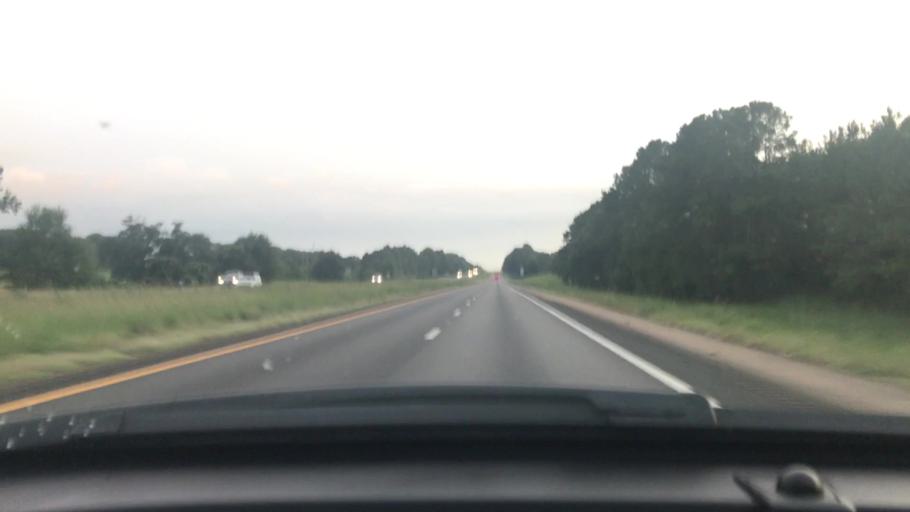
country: US
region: Louisiana
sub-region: Tangipahoa Parish
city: Kentwood
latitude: 31.0058
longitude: -90.5047
